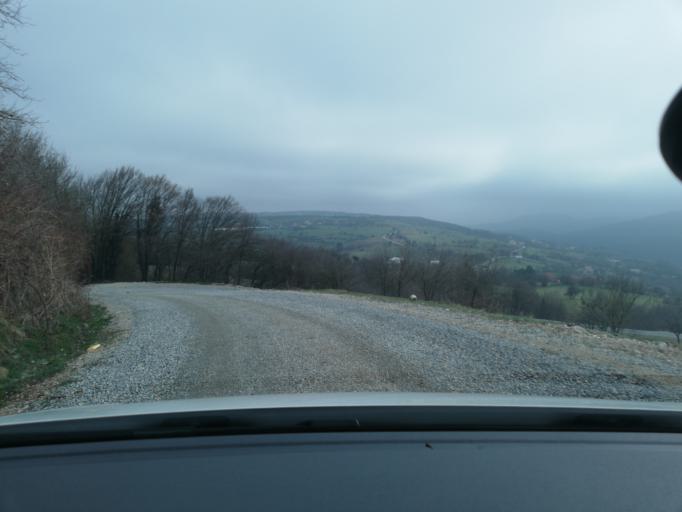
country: TR
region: Bolu
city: Bolu
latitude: 40.6674
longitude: 31.4618
